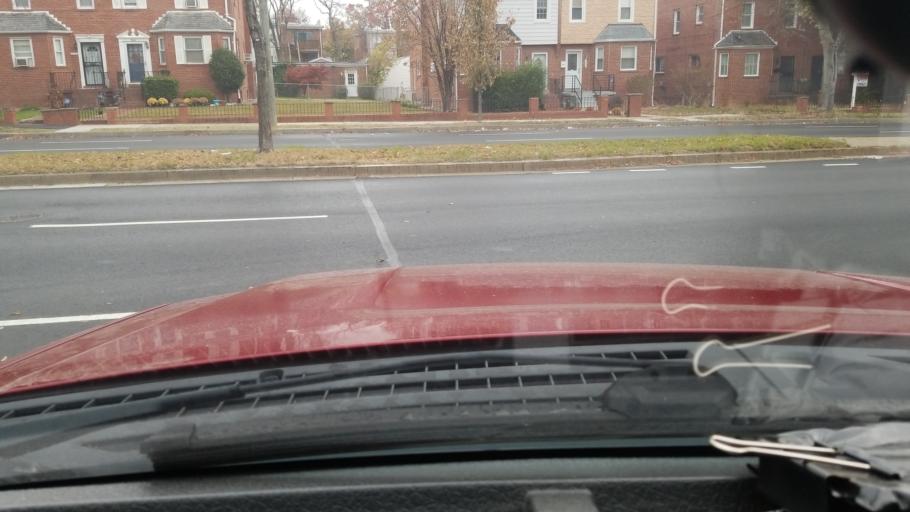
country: US
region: Maryland
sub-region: Prince George's County
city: Capitol Heights
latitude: 38.8896
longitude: -76.9239
